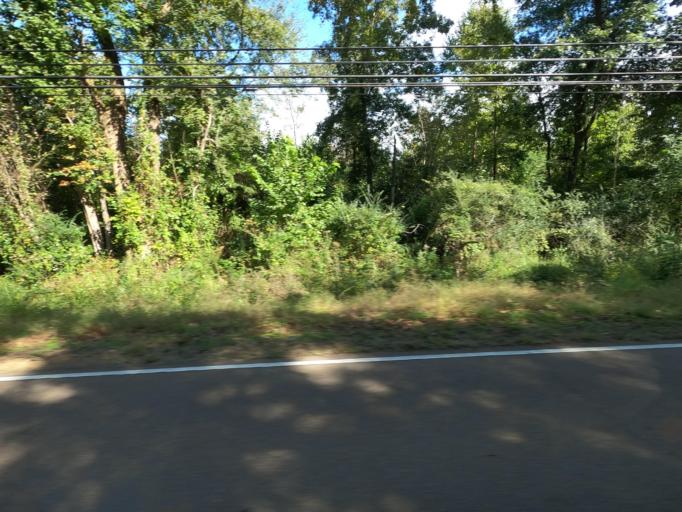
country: US
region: Tennessee
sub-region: Fayette County
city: Hickory Withe
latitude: 35.2256
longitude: -89.6503
